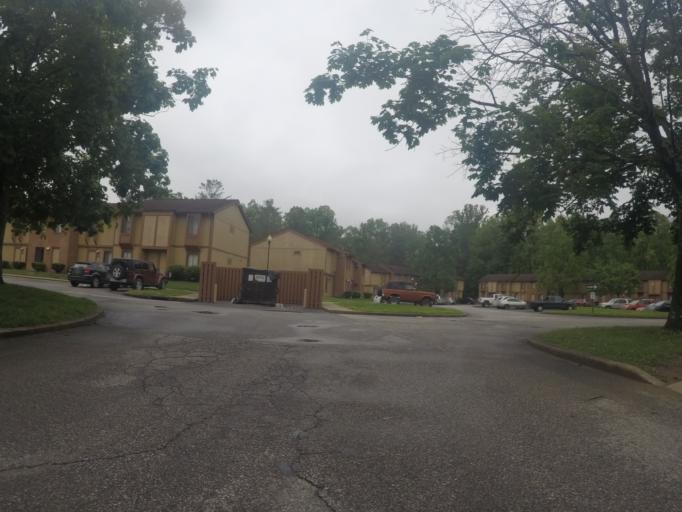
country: US
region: West Virginia
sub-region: Cabell County
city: Barboursville
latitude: 38.4256
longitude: -82.3040
